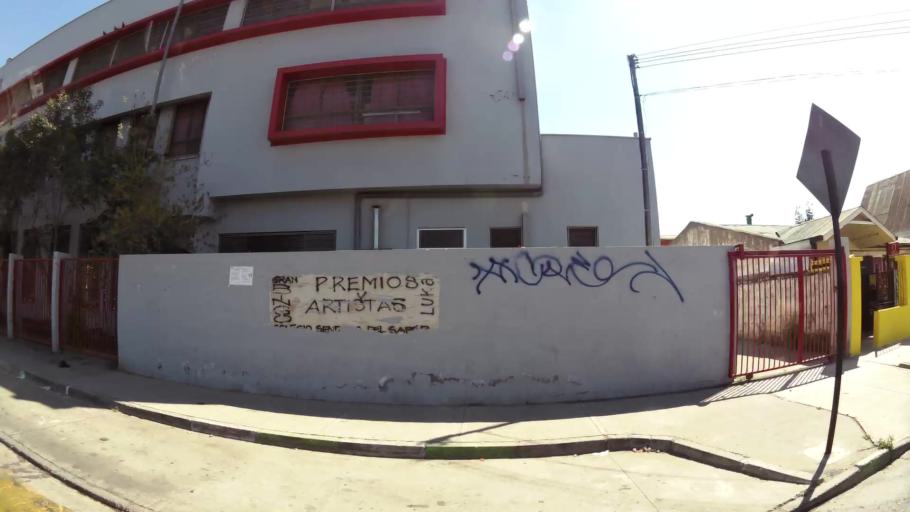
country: CL
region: Santiago Metropolitan
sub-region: Provincia de Santiago
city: La Pintana
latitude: -33.5264
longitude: -70.6385
